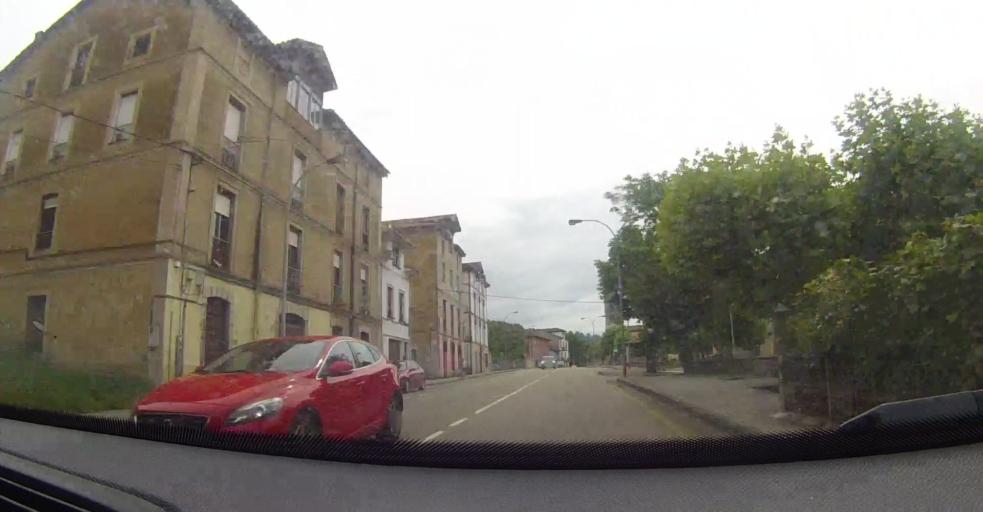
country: ES
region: Asturias
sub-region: Province of Asturias
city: Pilona
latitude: 43.3600
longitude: -5.3050
